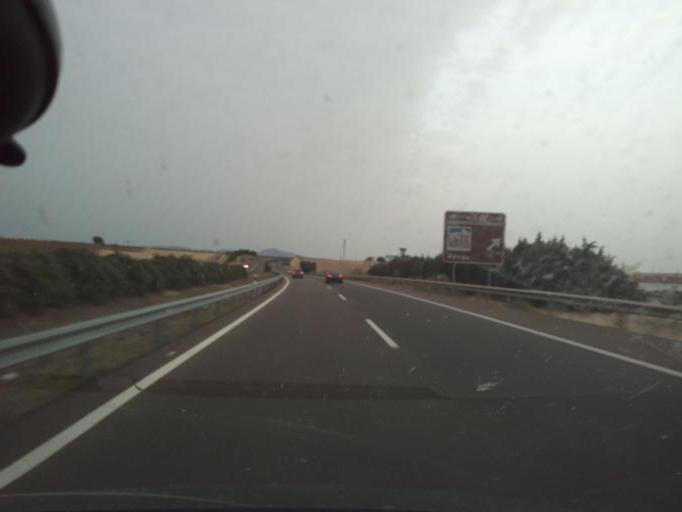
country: ES
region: Extremadura
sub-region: Provincia de Badajoz
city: Trujillanos
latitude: 38.9520
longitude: -6.2506
